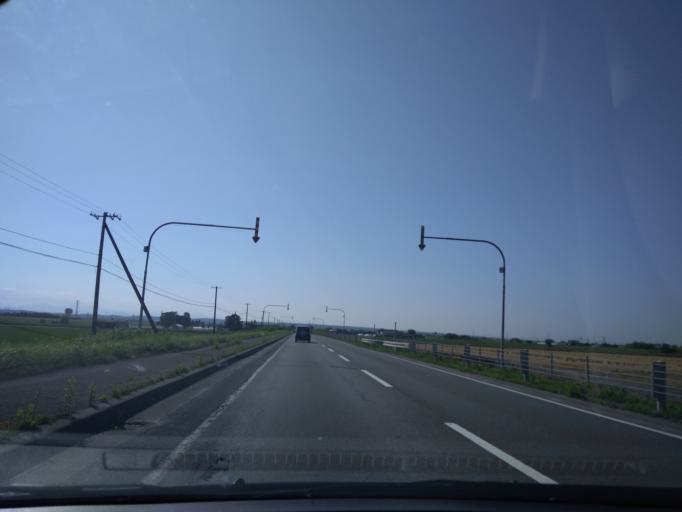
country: JP
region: Hokkaido
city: Kitahiroshima
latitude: 42.9922
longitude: 141.6020
